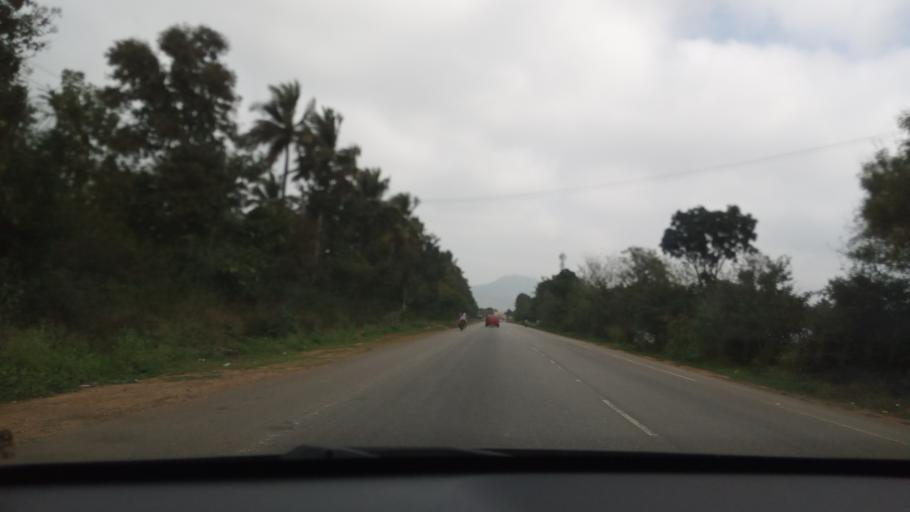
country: IN
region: Karnataka
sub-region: Chikkaballapur
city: Chintamani
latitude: 13.3124
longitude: 77.9784
